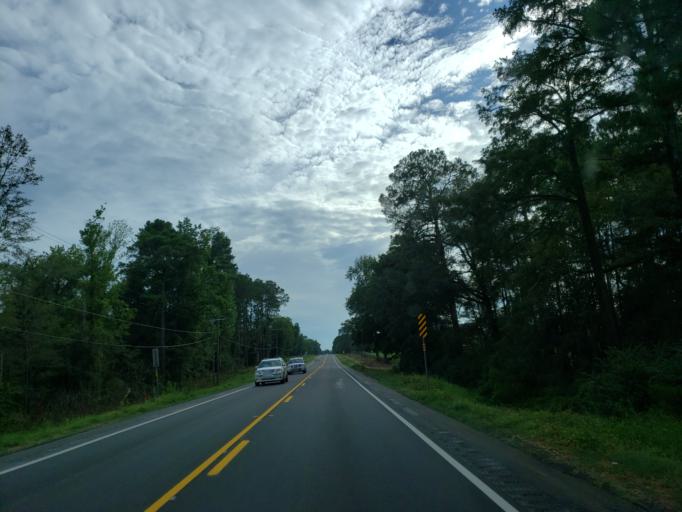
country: US
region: Georgia
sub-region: Irwin County
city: Ocilla
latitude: 31.5869
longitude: -83.2747
